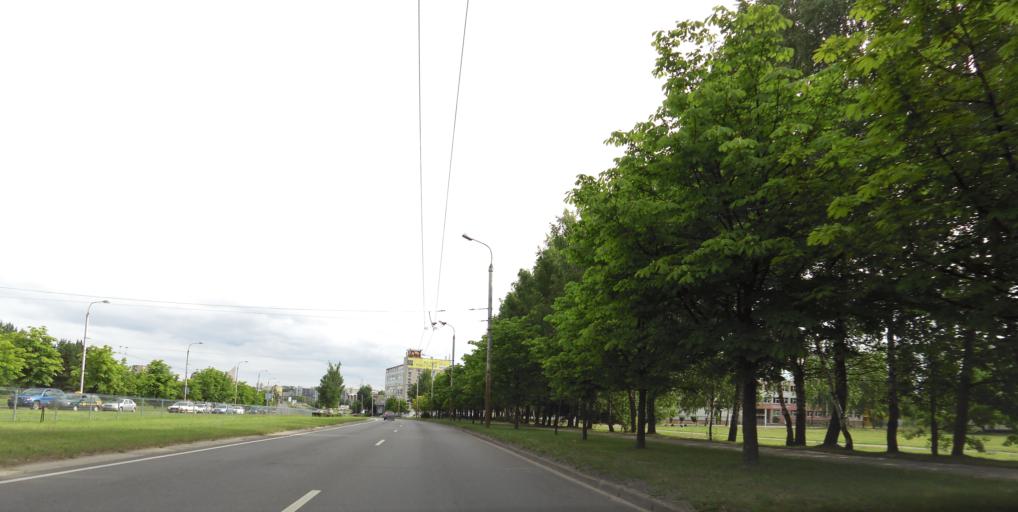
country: LT
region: Vilnius County
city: Justiniskes
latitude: 54.7129
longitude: 25.2288
